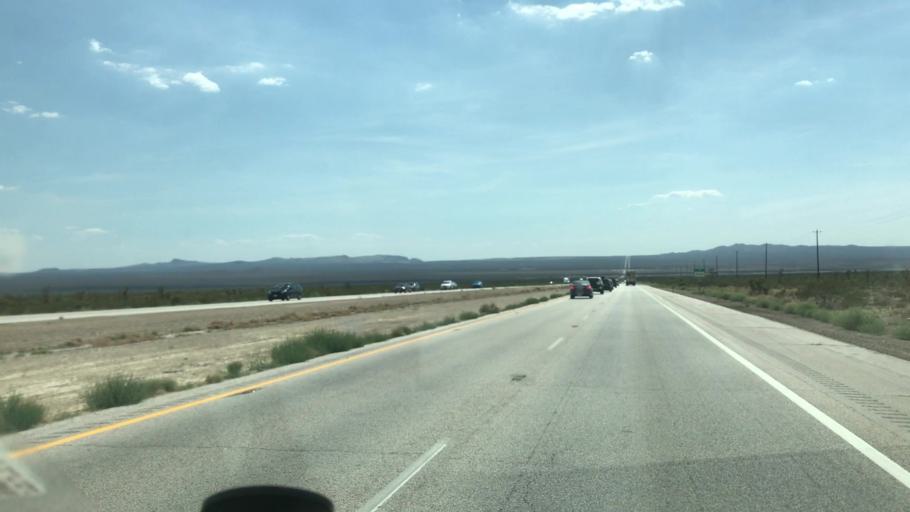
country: US
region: Nevada
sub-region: Clark County
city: Sandy Valley
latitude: 35.4628
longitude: -115.6217
